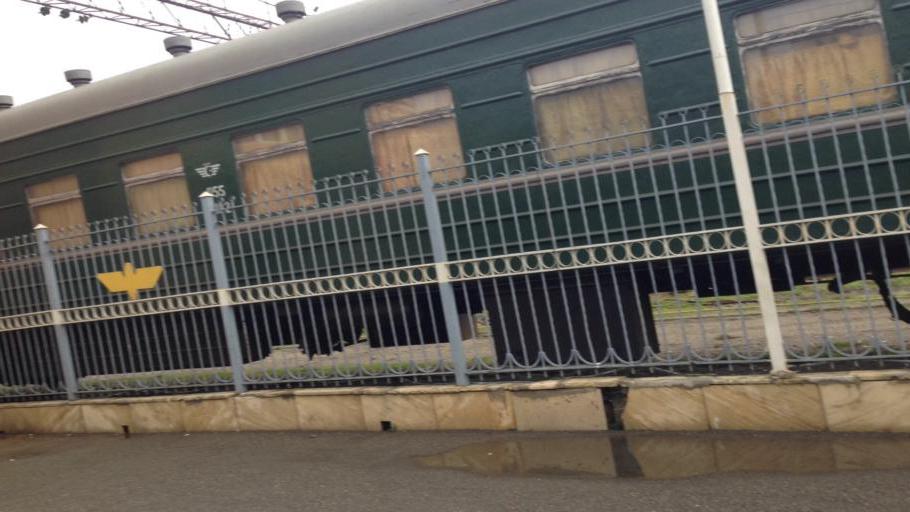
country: AZ
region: Baki
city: Baku
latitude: 40.3843
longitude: 49.8551
